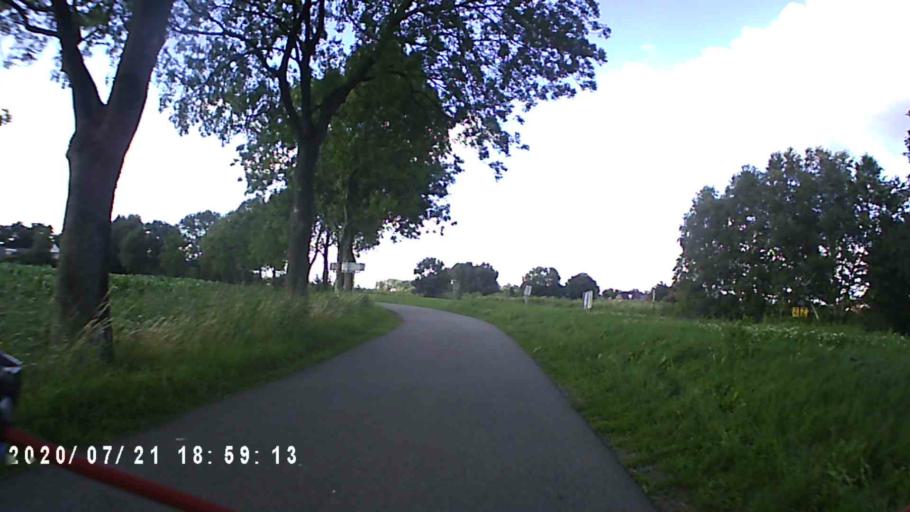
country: NL
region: Groningen
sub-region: Gemeente Hoogezand-Sappemeer
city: Hoogezand
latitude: 53.2194
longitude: 6.7391
